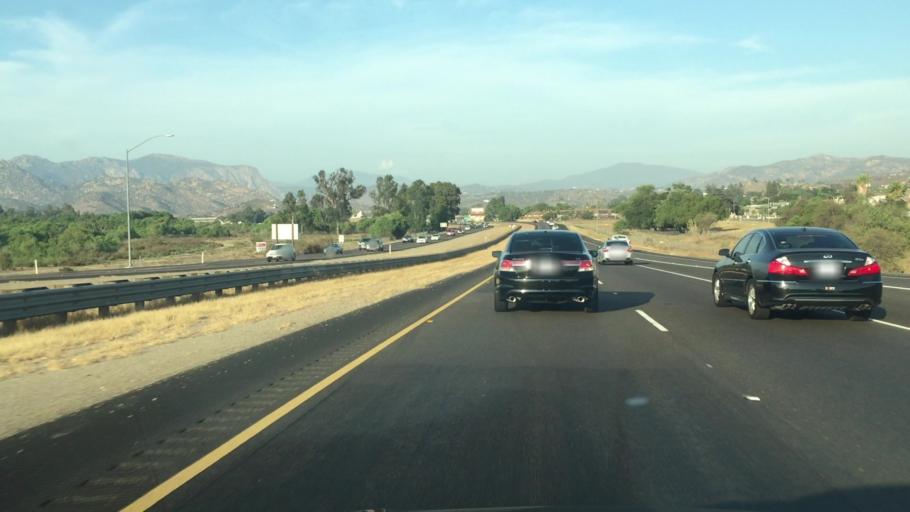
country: US
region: California
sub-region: San Diego County
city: Lakeside
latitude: 32.8554
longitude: -116.9445
